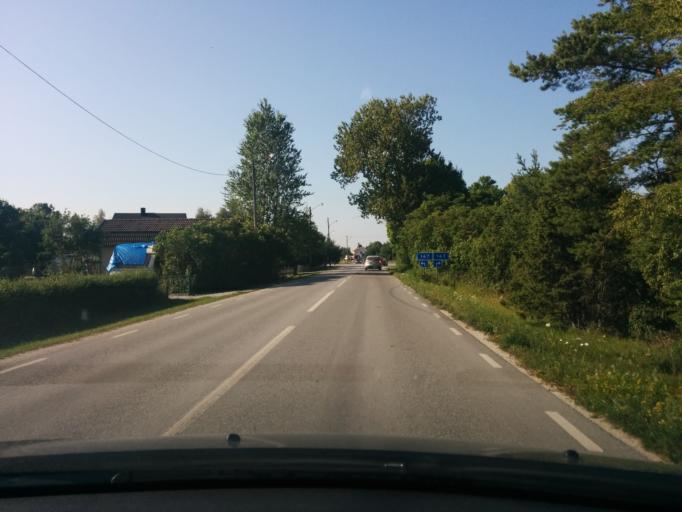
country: SE
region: Gotland
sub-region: Gotland
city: Slite
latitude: 57.6797
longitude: 18.7676
